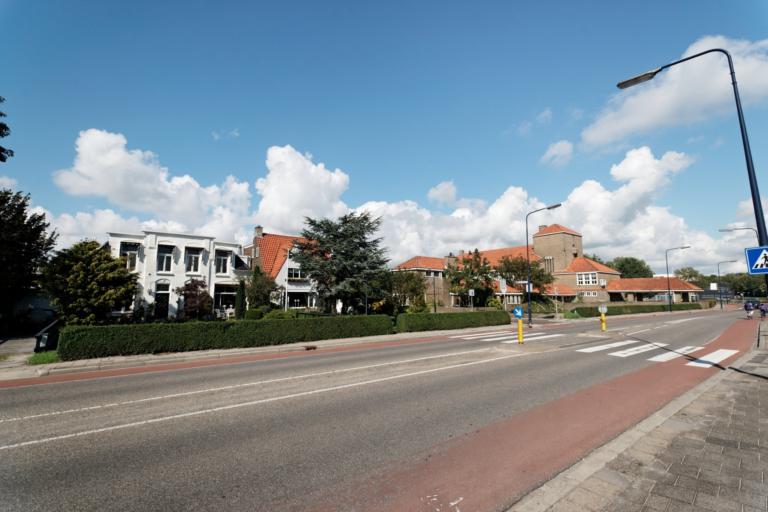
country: NL
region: Friesland
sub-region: Gemeente Harlingen
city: Harlingen
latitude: 53.1708
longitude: 5.4258
